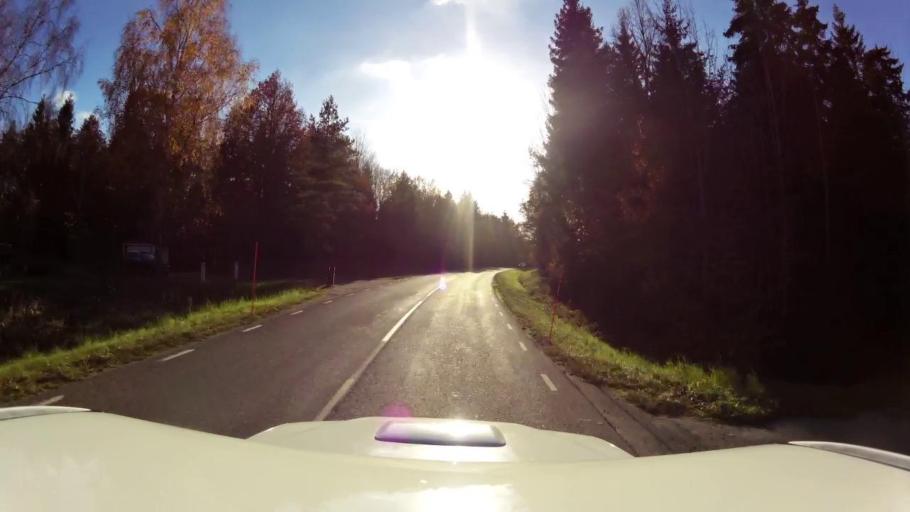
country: SE
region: OEstergoetland
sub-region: Linkopings Kommun
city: Vikingstad
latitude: 58.3171
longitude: 15.4957
